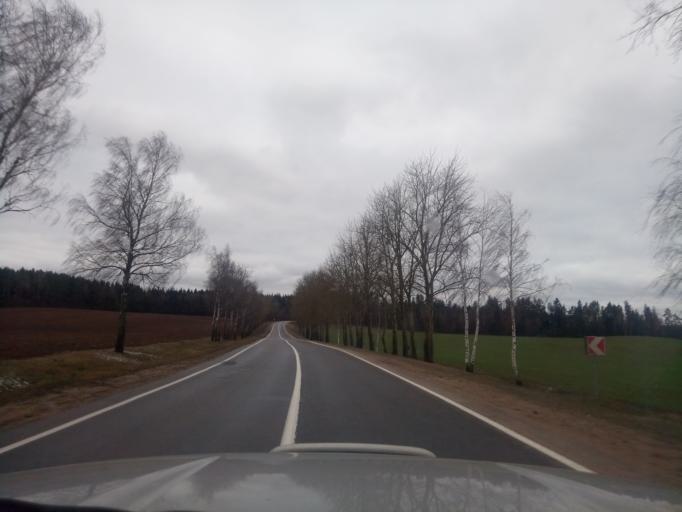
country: BY
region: Minsk
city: Kapyl'
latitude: 53.1673
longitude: 27.1239
